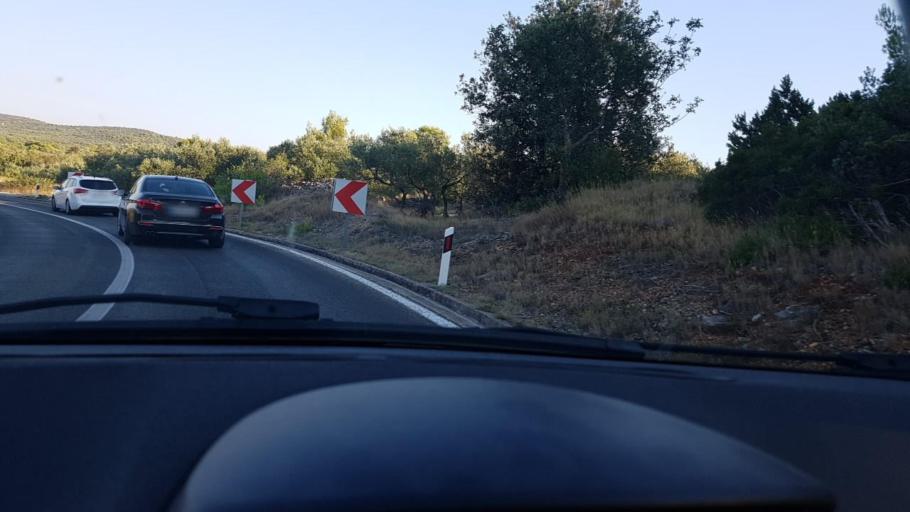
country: HR
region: Sibensko-Kniniska
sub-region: Grad Sibenik
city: Tisno
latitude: 43.7918
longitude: 15.6256
